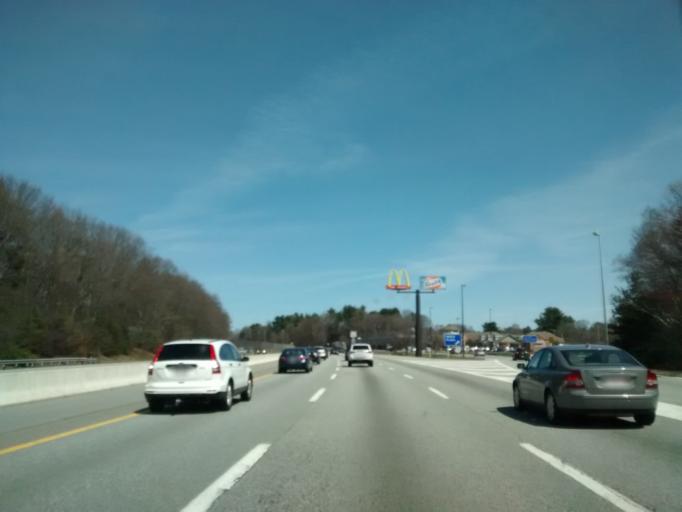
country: US
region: Massachusetts
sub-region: Middlesex County
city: Cochituate
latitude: 42.3112
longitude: -71.3682
